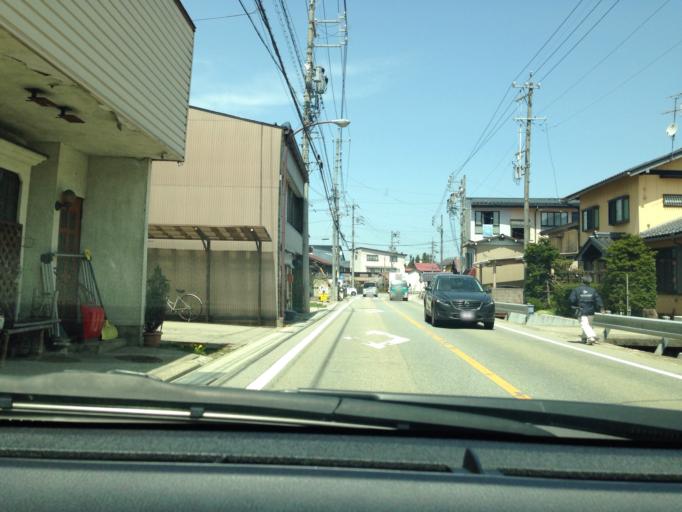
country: JP
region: Gifu
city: Takayama
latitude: 36.1304
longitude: 137.2558
